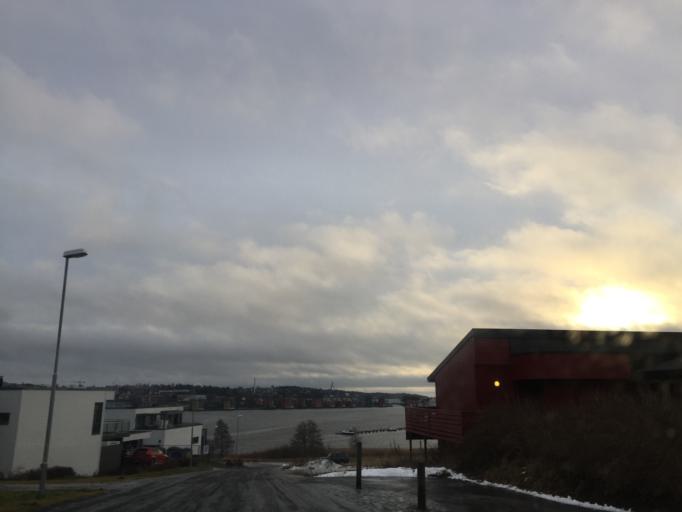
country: NO
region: Ostfold
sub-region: Moss
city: Moss
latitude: 59.4463
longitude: 10.6525
